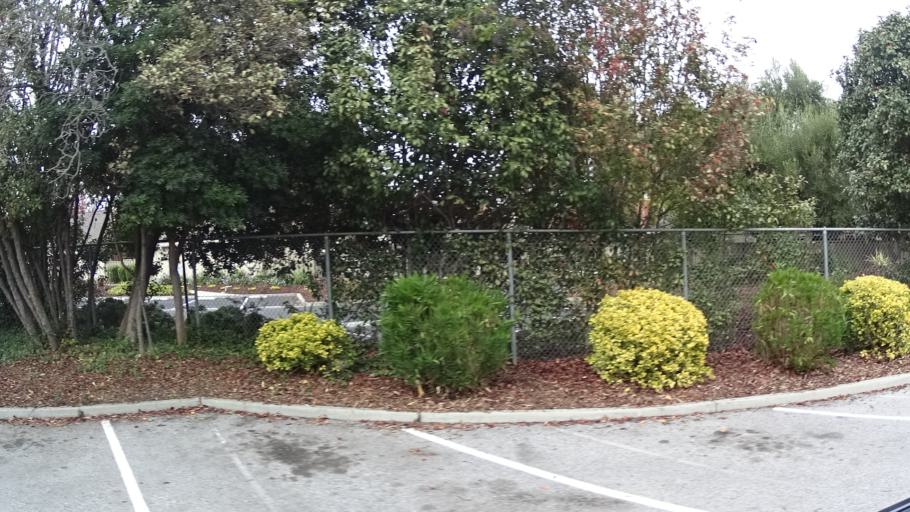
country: US
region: California
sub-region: Santa Clara County
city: Sunnyvale
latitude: 37.3666
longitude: -122.0385
